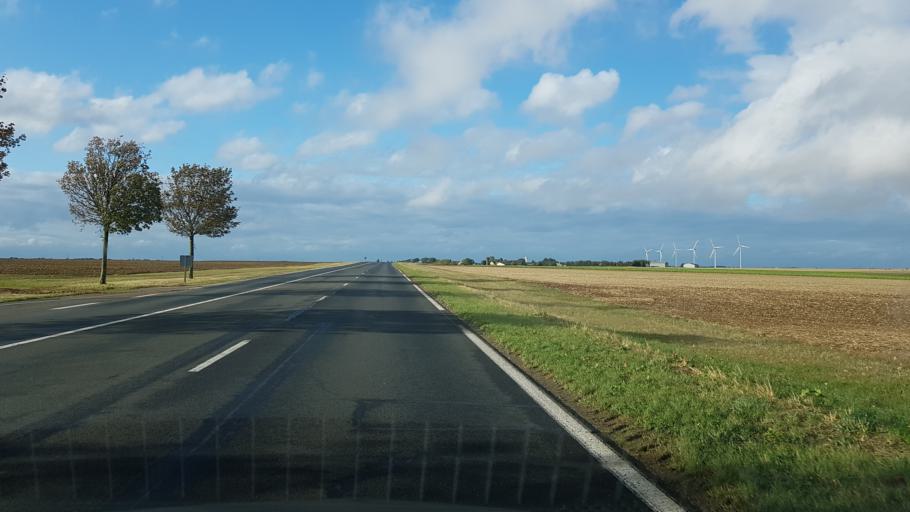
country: FR
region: Centre
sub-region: Departement du Loiret
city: Sermaises
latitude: 48.2494
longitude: 2.2161
